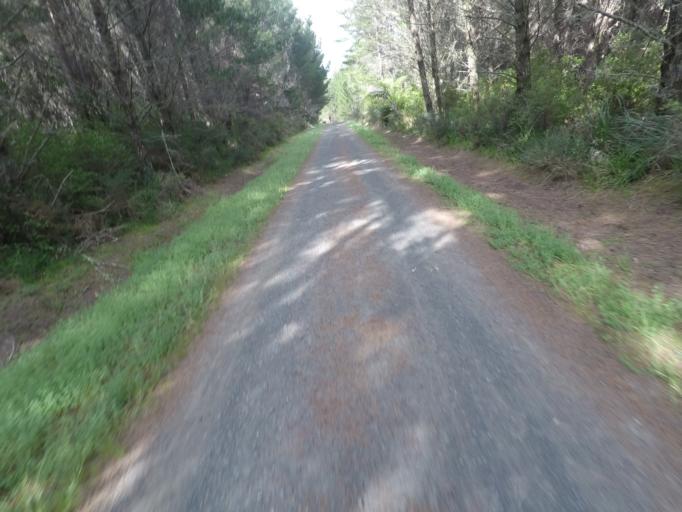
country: NZ
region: Auckland
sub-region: Auckland
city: Muriwai Beach
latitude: -36.7436
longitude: 174.5672
